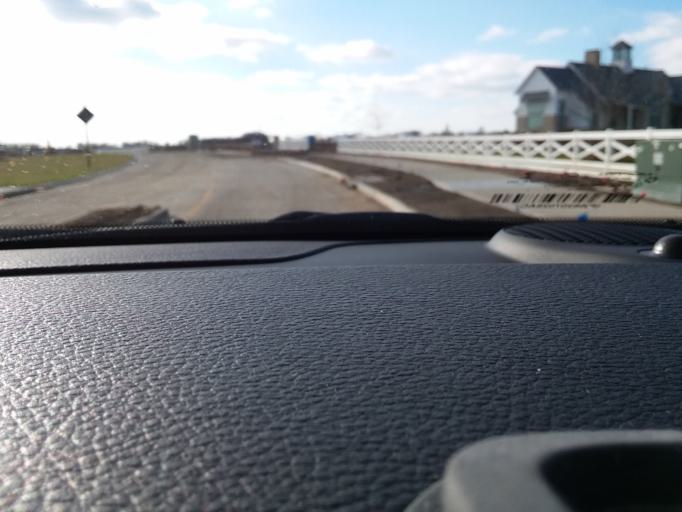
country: US
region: Texas
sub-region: Denton County
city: Krugerville
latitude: 33.2653
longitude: -96.8977
